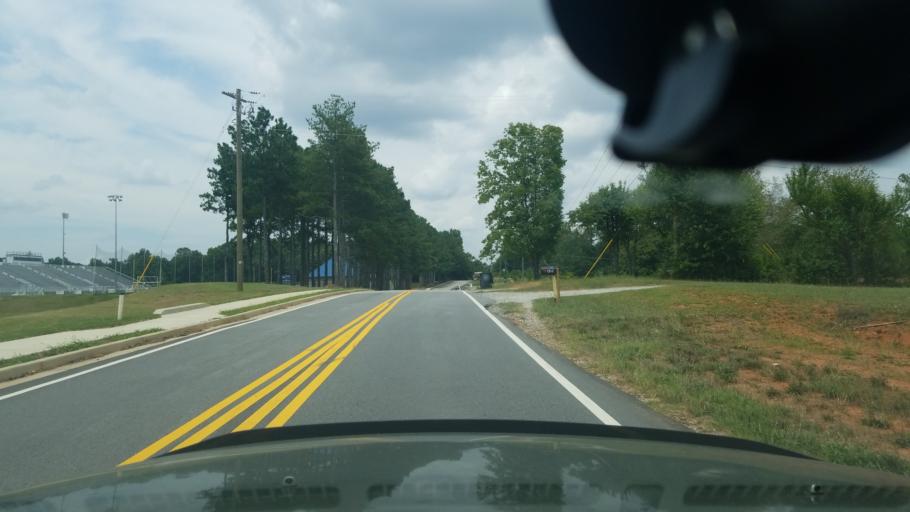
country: US
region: Georgia
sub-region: Fulton County
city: Milton
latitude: 34.1460
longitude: -84.2249
